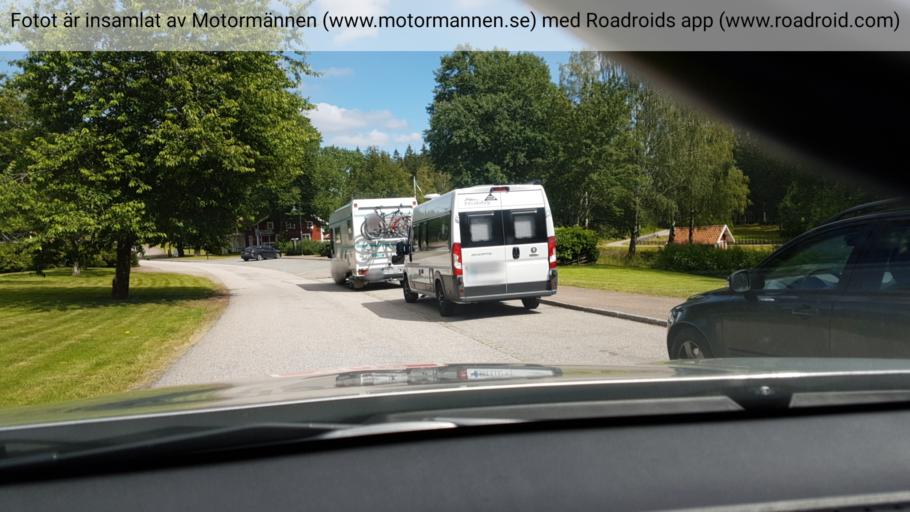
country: SE
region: Vaestra Goetaland
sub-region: Boras Kommun
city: Sandared
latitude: 57.6848
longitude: 12.7831
